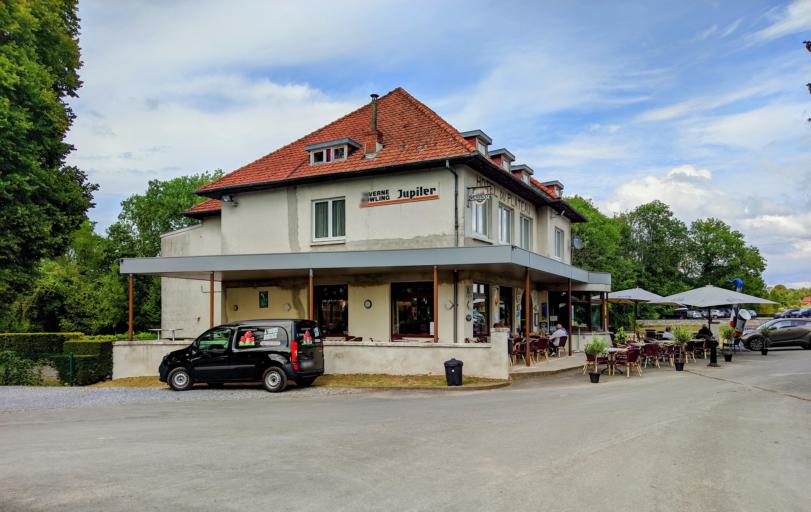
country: BE
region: Wallonia
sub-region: Province de Namur
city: Dinant
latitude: 50.2616
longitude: 4.9157
